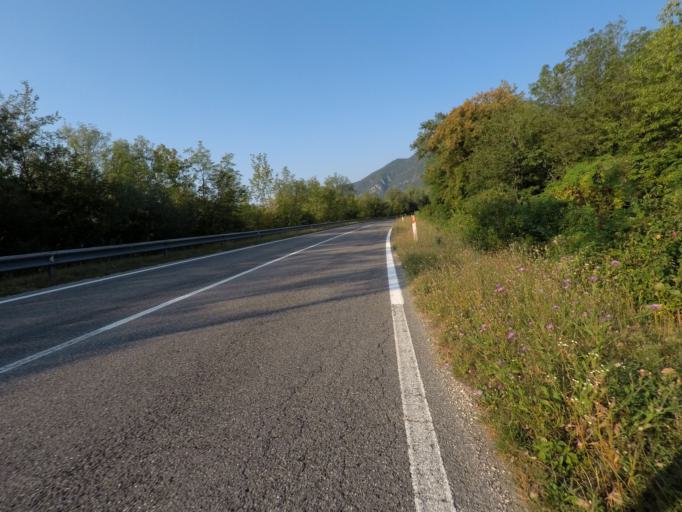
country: IT
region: Friuli Venezia Giulia
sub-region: Provincia di Udine
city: Trasaghis
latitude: 46.2693
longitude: 13.0549
